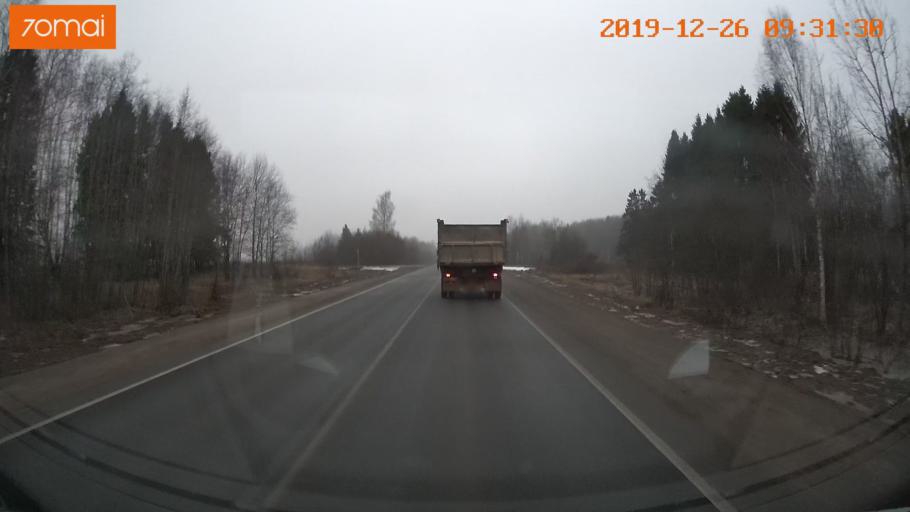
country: RU
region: Vologda
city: Gryazovets
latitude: 59.0697
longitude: 40.1272
